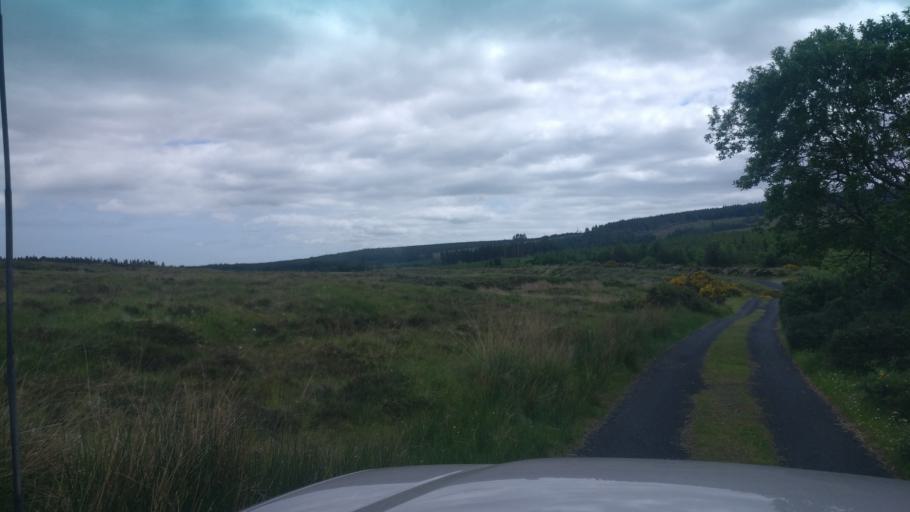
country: IE
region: Connaught
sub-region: County Galway
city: Loughrea
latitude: 53.1130
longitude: -8.6302
